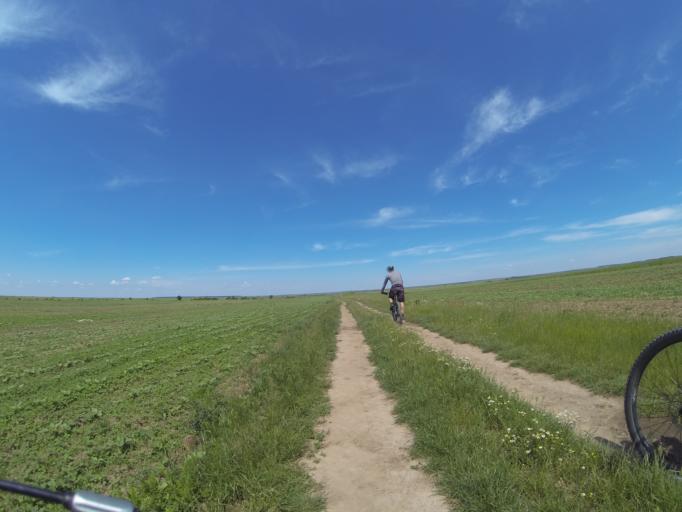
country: RO
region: Dolj
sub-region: Comuna Teslui
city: Teslui
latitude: 44.1947
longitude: 24.1388
